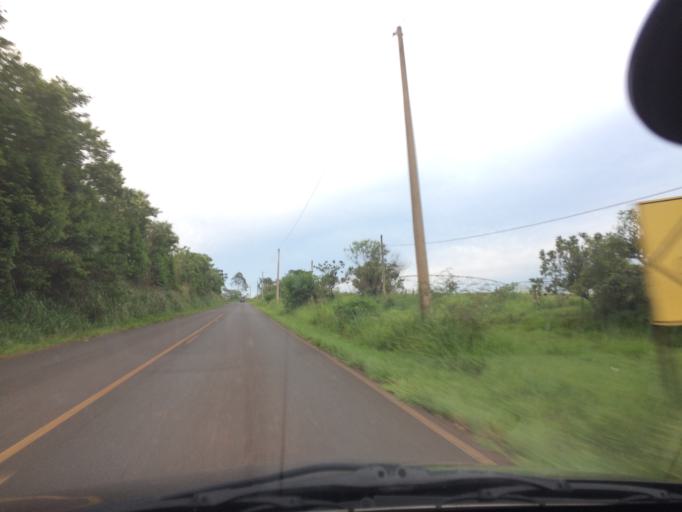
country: BR
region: Sao Paulo
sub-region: Casa Branca
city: Casa Branca
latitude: -21.7629
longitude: -47.1056
